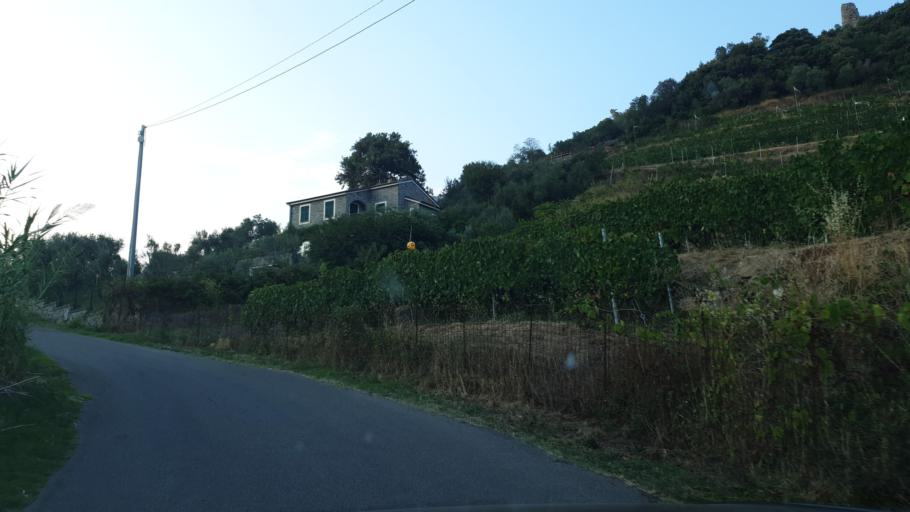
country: IT
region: Liguria
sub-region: Provincia di La Spezia
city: Bonassola
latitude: 44.1910
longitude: 9.5833
